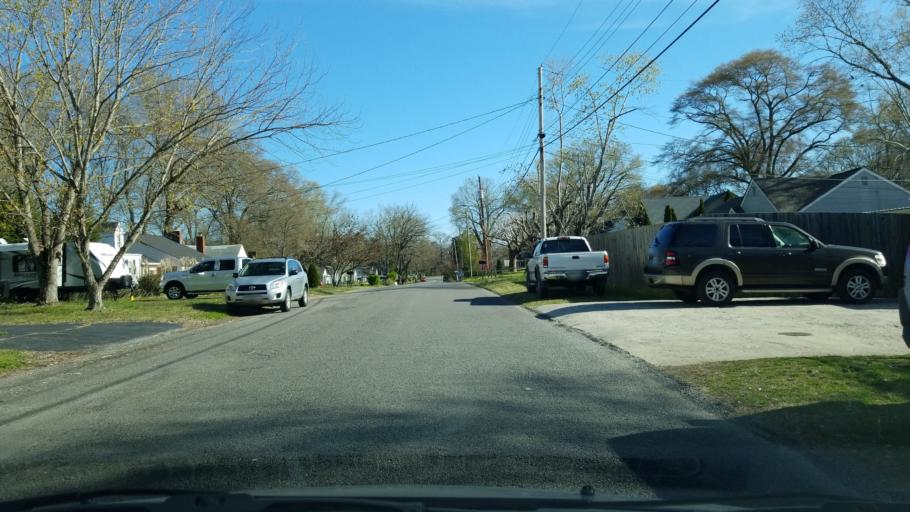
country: US
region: Tennessee
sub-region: Hamilton County
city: East Ridge
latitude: 35.0140
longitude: -85.2263
